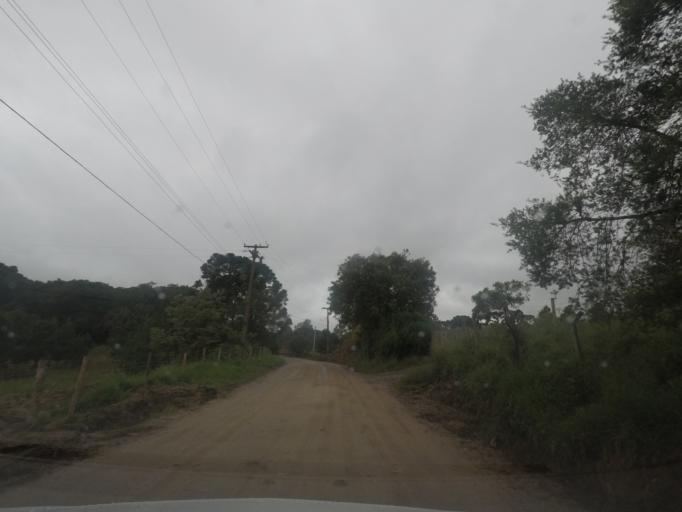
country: BR
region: Parana
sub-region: Campina Grande Do Sul
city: Campina Grande do Sul
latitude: -25.3058
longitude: -49.1103
